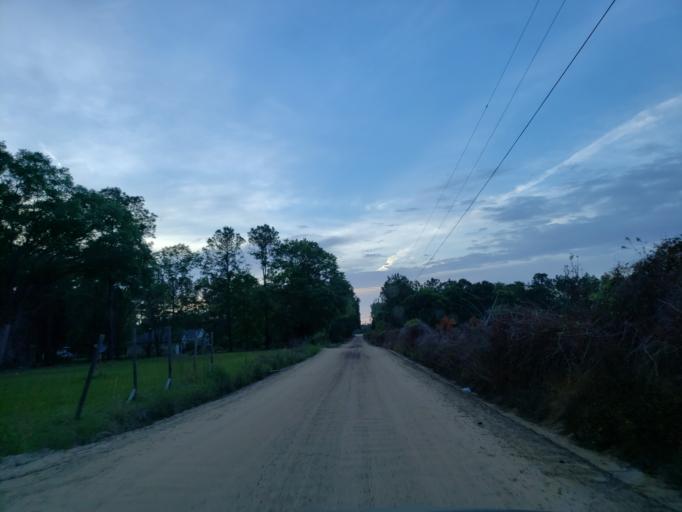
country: US
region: Georgia
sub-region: Lowndes County
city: Hahira
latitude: 30.9709
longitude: -83.3952
